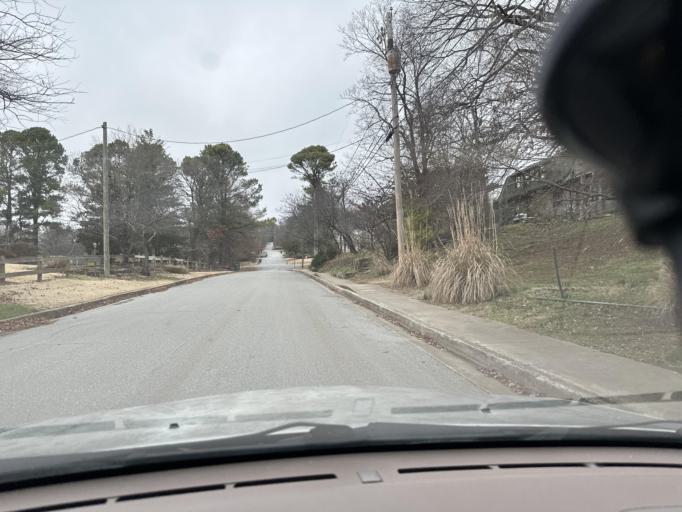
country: US
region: Arkansas
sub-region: Washington County
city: Fayetteville
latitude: 36.0730
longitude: -94.1544
